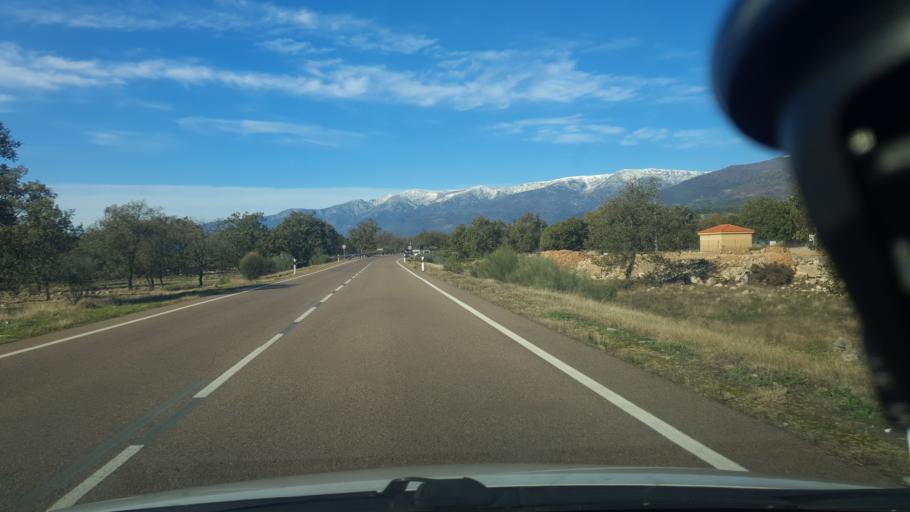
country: ES
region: Castille and Leon
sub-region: Provincia de Avila
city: Candeleda
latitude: 40.1400
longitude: -5.2566
